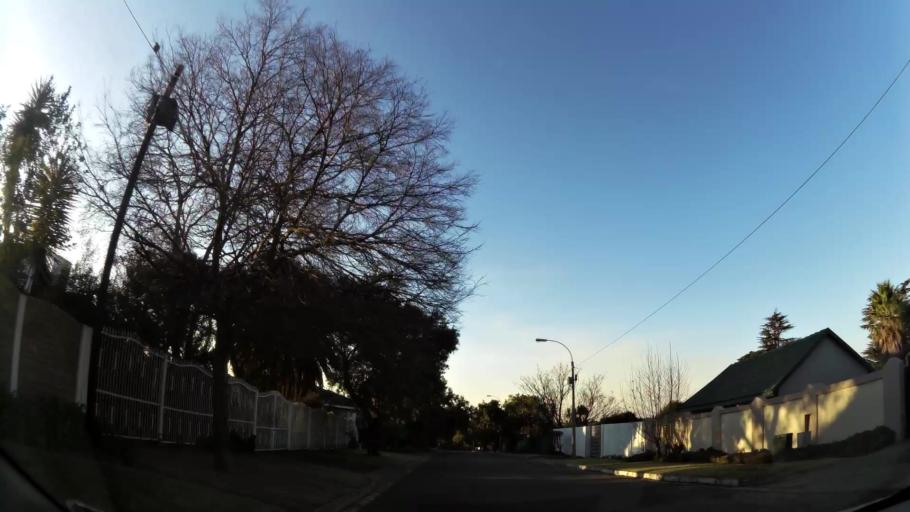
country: ZA
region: Gauteng
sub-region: City of Johannesburg Metropolitan Municipality
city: Roodepoort
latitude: -26.1543
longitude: 27.8988
